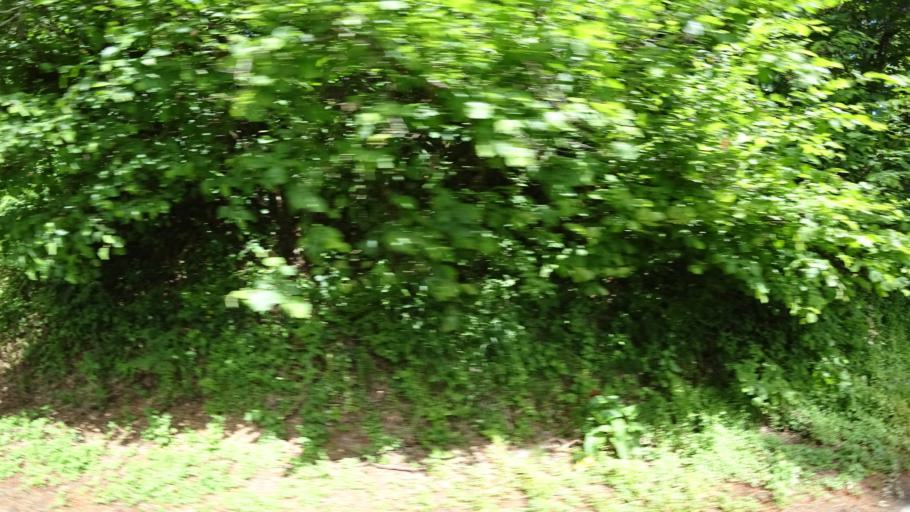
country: US
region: Oregon
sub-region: Washington County
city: Oak Hills
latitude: 45.5868
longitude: -122.8055
